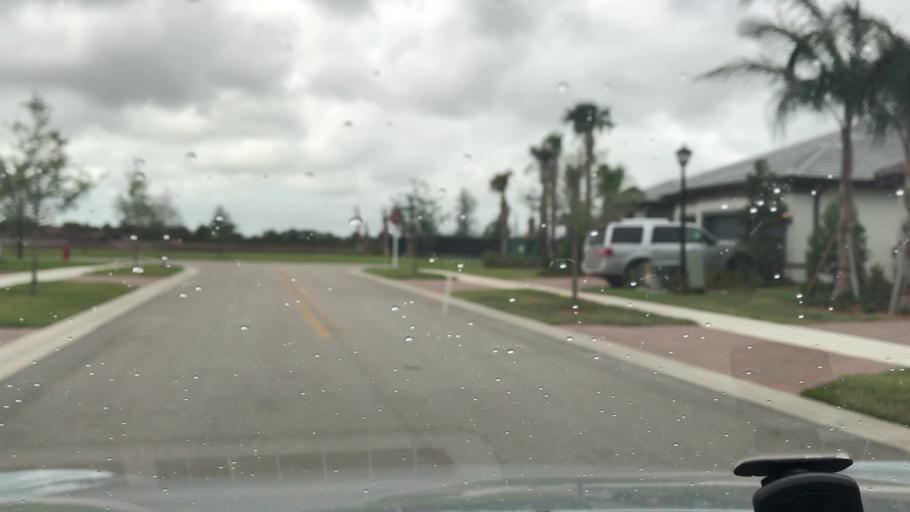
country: US
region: Florida
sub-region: Indian River County
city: Gifford
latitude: 27.6850
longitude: -80.4325
